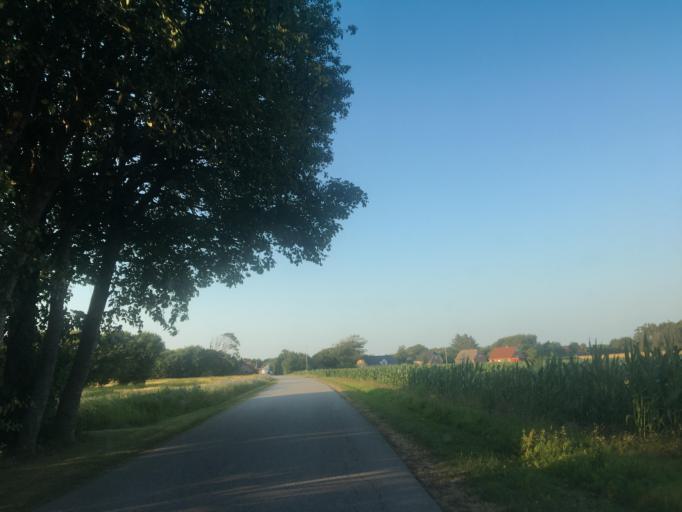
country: DK
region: North Denmark
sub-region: Thisted Kommune
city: Hurup
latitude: 56.8427
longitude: 8.3596
